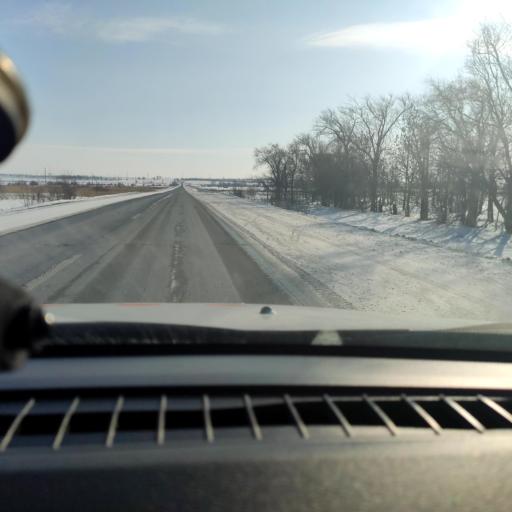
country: RU
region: Samara
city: Smyshlyayevka
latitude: 53.1677
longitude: 50.4569
